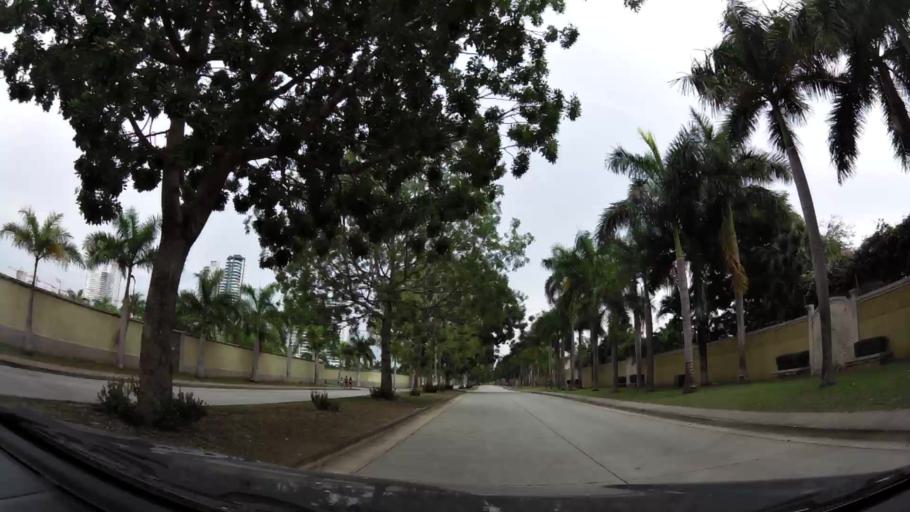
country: PA
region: Panama
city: San Miguelito
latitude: 9.0131
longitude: -79.4617
